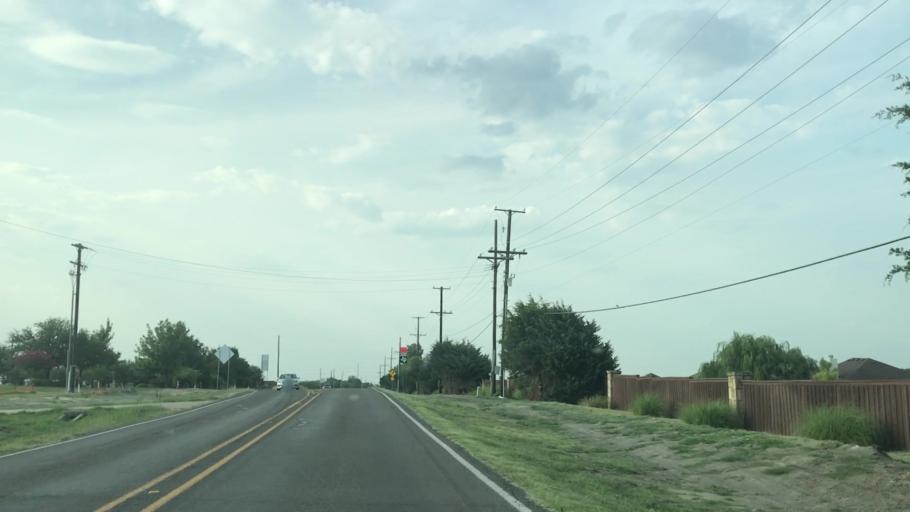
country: US
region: Texas
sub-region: Rockwall County
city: Fate
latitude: 32.9267
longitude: -96.4183
